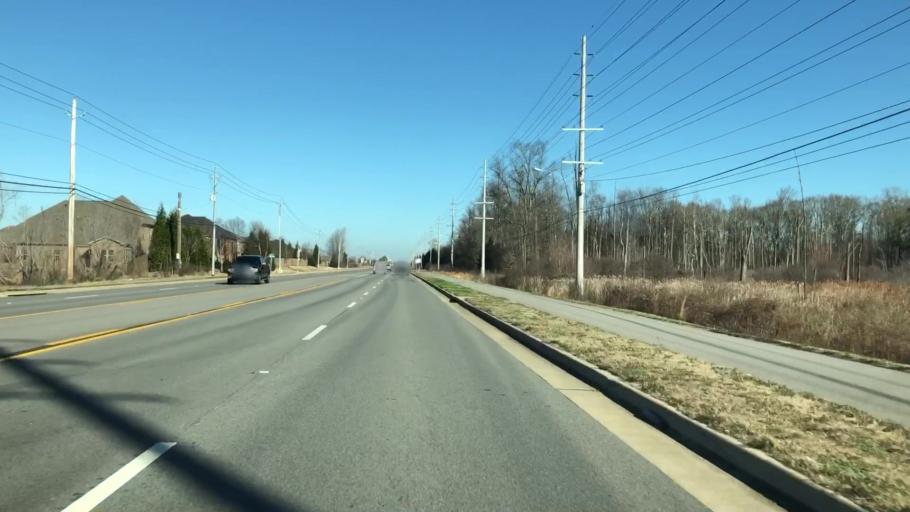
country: US
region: Alabama
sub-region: Madison County
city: Madison
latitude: 34.7220
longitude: -86.7864
